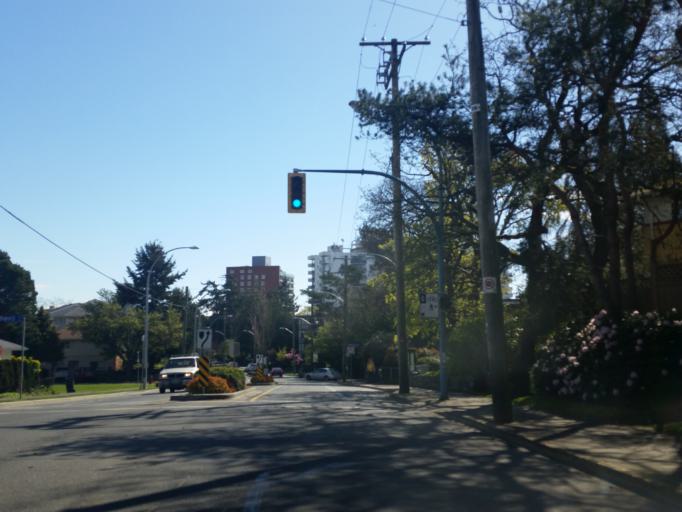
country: CA
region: British Columbia
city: Victoria
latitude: 48.4316
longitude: -123.3938
